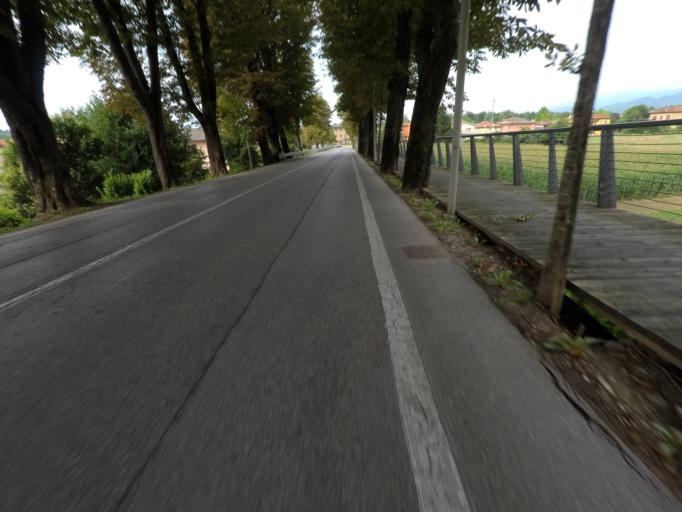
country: IT
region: Veneto
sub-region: Provincia di Treviso
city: Cappella Maggiore
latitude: 45.9686
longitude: 12.3560
